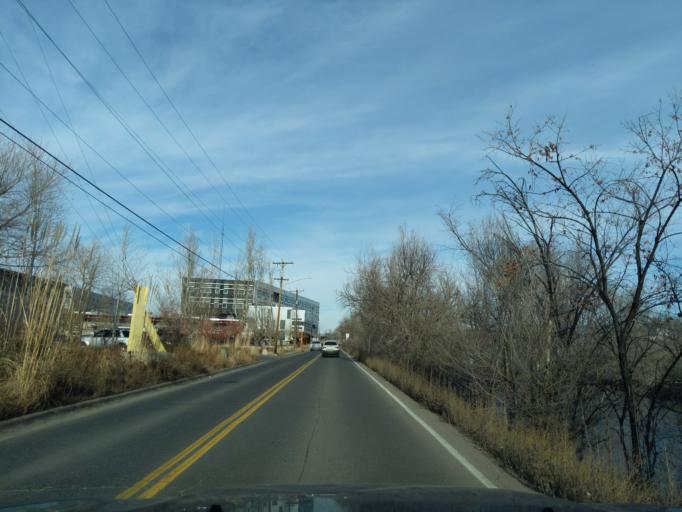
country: US
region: Colorado
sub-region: Denver County
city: Denver
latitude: 39.7719
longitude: -104.9816
